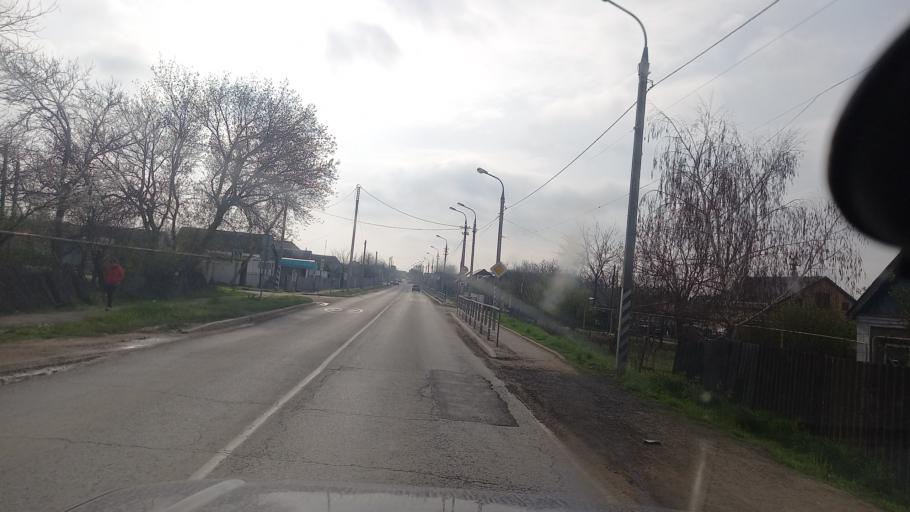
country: RU
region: Krasnodarskiy
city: Varenikovskaya
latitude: 45.1123
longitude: 37.6428
